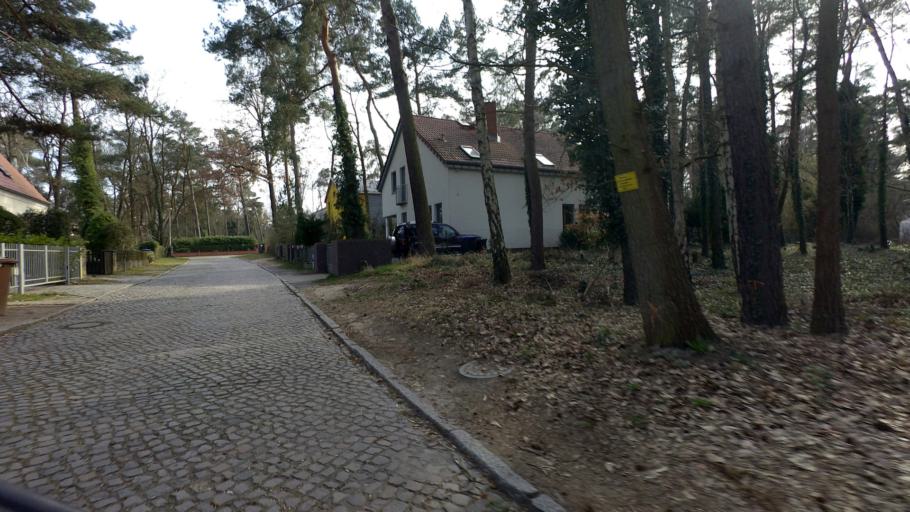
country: DE
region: Berlin
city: Nikolassee
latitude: 52.4122
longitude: 13.2026
